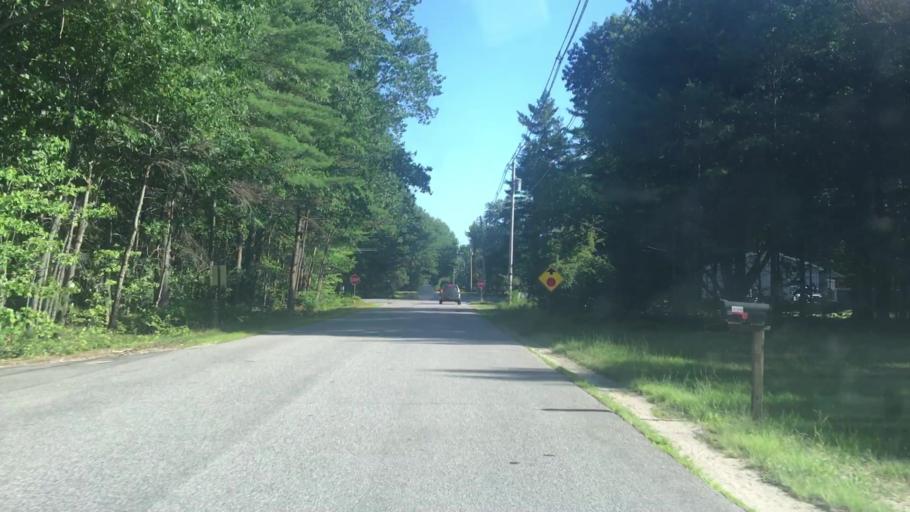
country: US
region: Maine
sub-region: Cumberland County
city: Gorham
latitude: 43.7285
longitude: -70.5162
